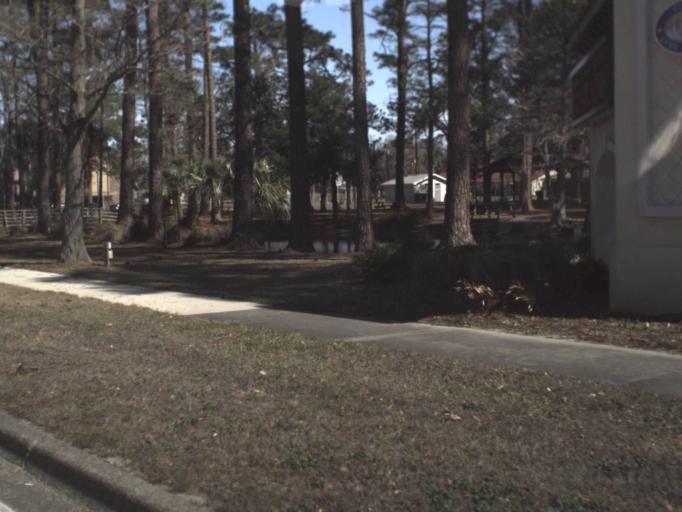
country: US
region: Florida
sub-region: Bay County
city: Lynn Haven
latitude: 30.2439
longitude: -85.6486
